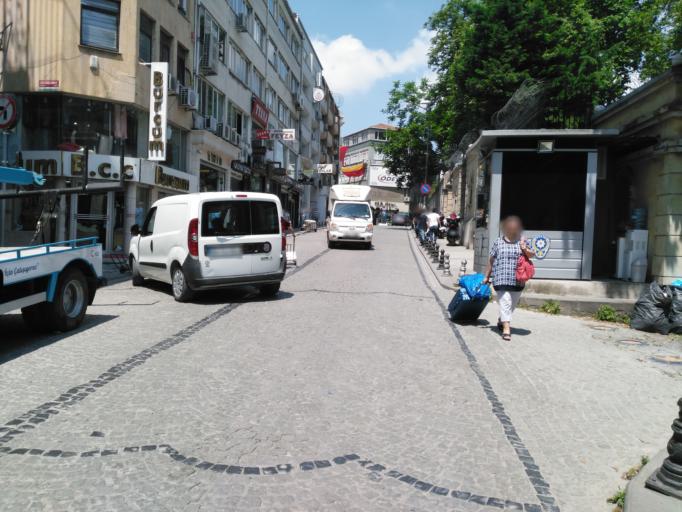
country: TR
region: Istanbul
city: Eminoenue
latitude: 41.0112
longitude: 28.9743
